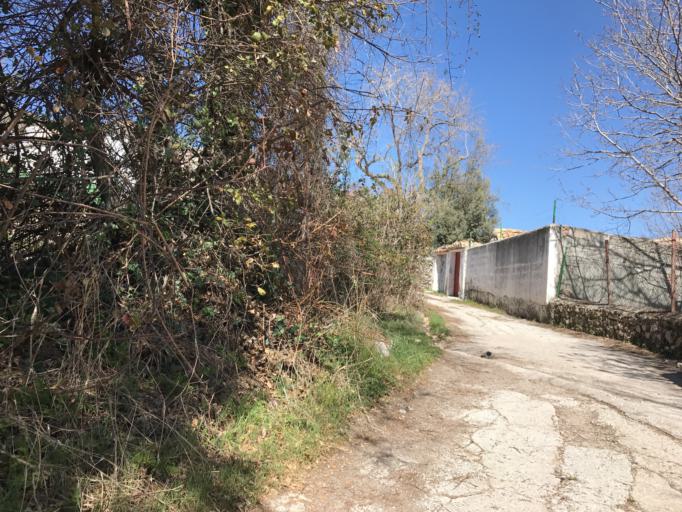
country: ES
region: Andalusia
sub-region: Provincia de Granada
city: Iznalloz
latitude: 37.3208
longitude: -3.4527
